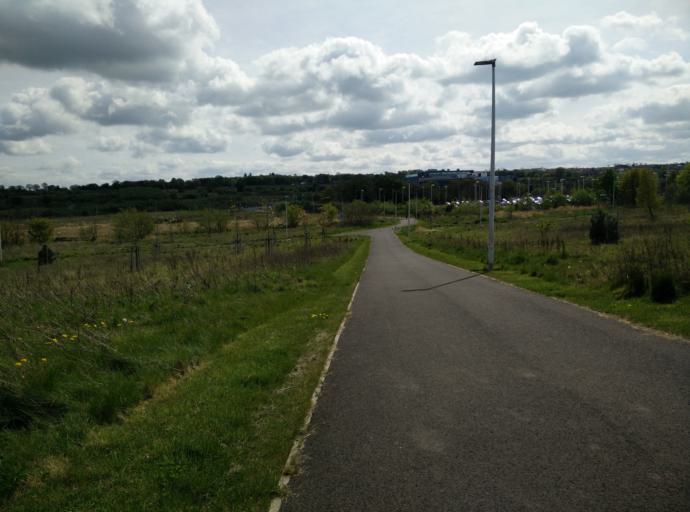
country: GB
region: Scotland
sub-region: West Lothian
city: Seafield
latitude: 55.9260
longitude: -3.1322
